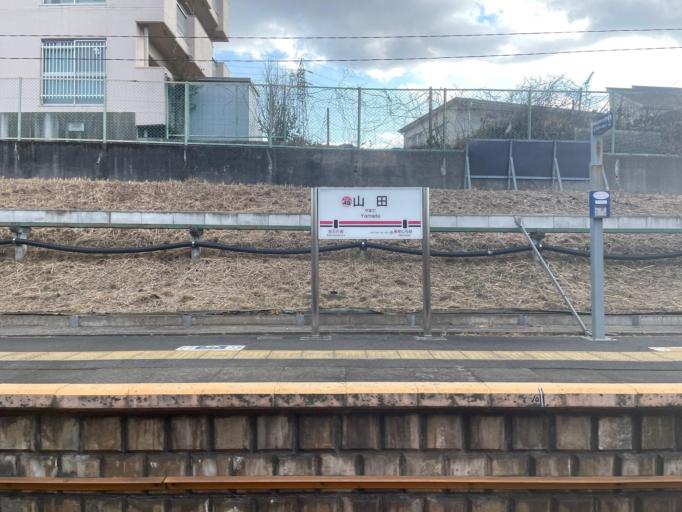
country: JP
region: Tokyo
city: Hachioji
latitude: 35.6444
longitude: 139.3202
